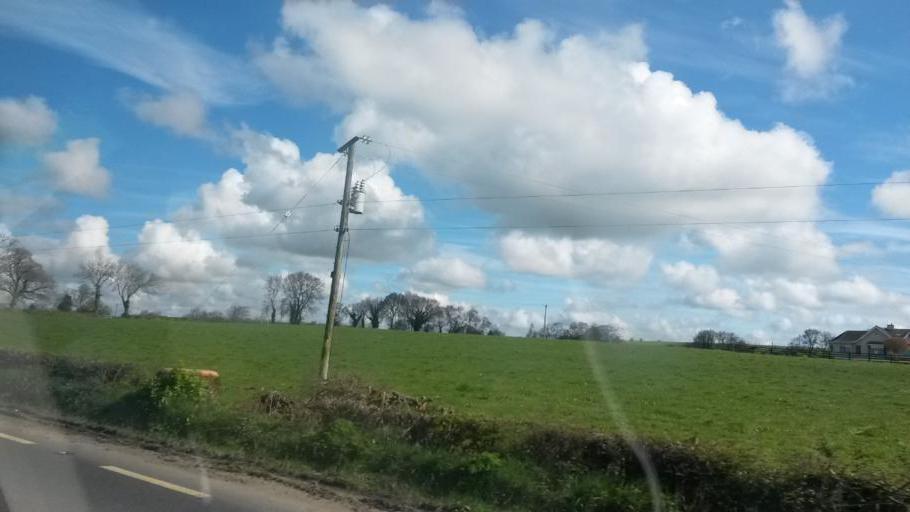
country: IE
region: Ulster
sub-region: An Cabhan
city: Virginia
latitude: 53.8100
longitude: -7.0437
